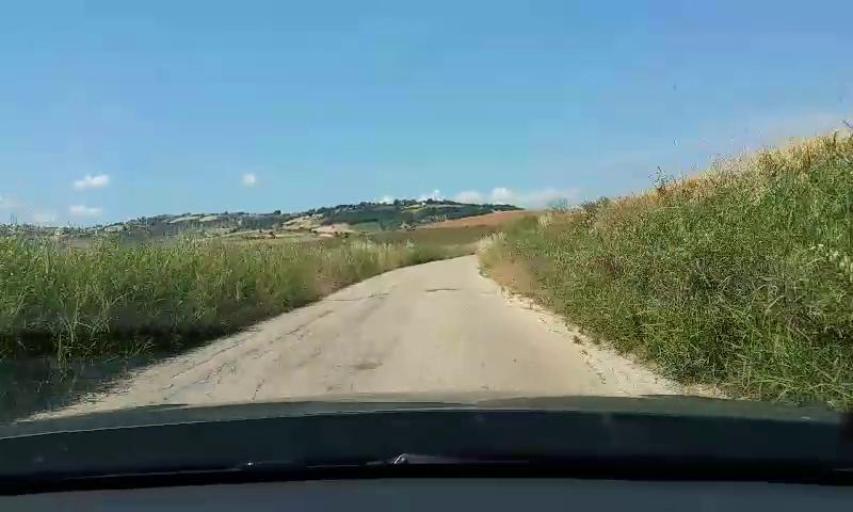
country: IT
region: Molise
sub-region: Provincia di Campobasso
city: Montecilfone
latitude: 41.9205
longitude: 14.8417
